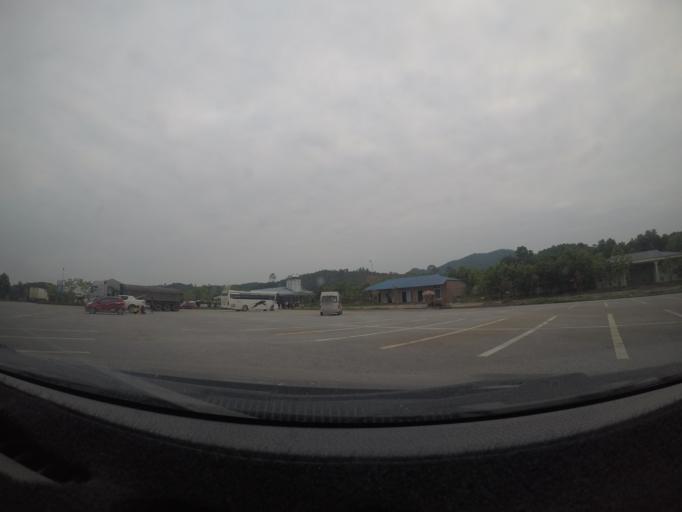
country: VN
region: Yen Bai
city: Yen Bai
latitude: 21.6743
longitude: 104.8780
